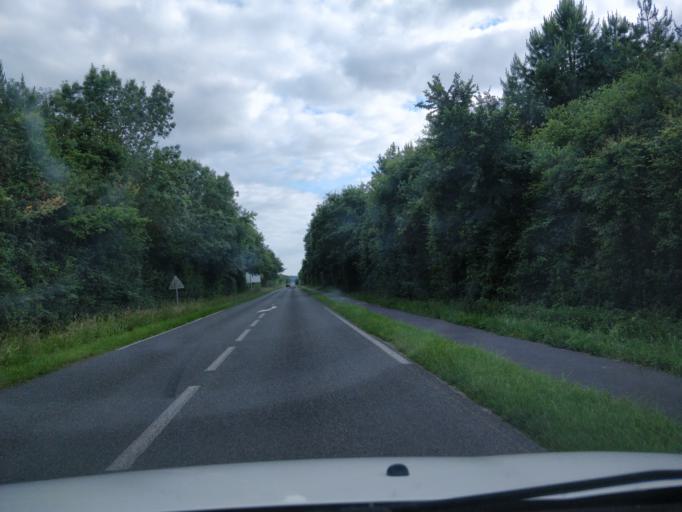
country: FR
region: Pays de la Loire
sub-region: Departement de Maine-et-Loire
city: Feneu
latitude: 47.5640
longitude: -0.5973
